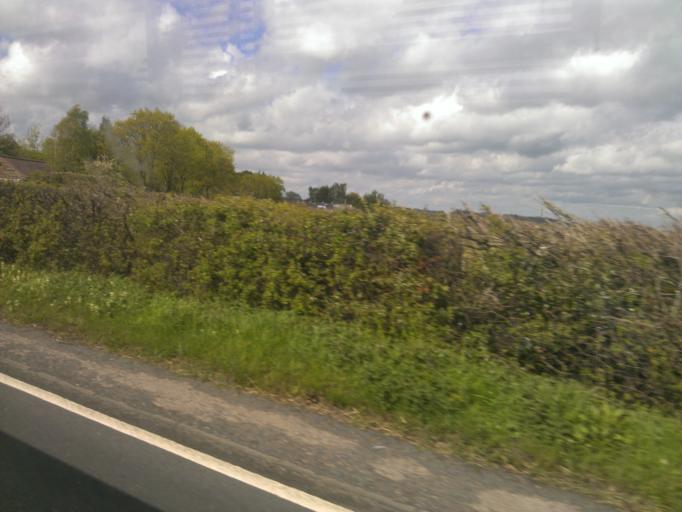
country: GB
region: England
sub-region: Essex
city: Eight Ash Green
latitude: 51.9013
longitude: 0.8076
